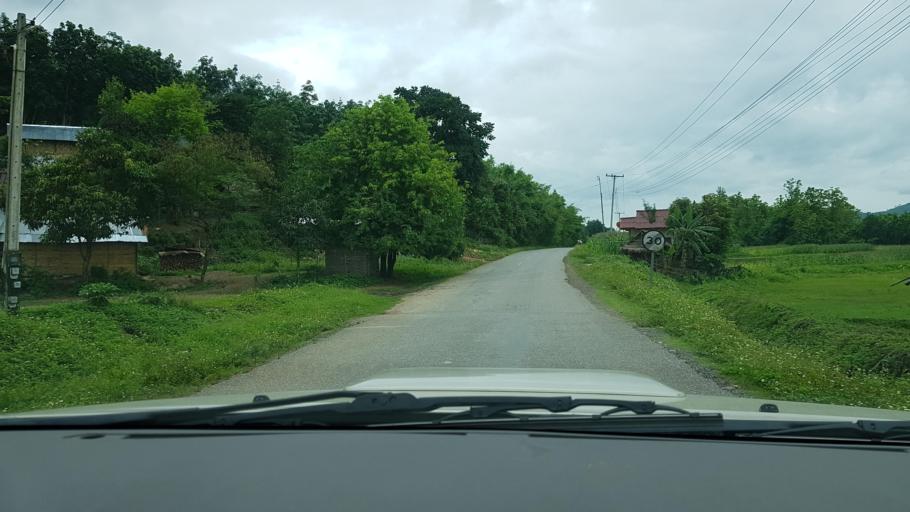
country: LA
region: Loungnamtha
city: Muang Nale
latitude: 20.2715
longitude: 101.6024
